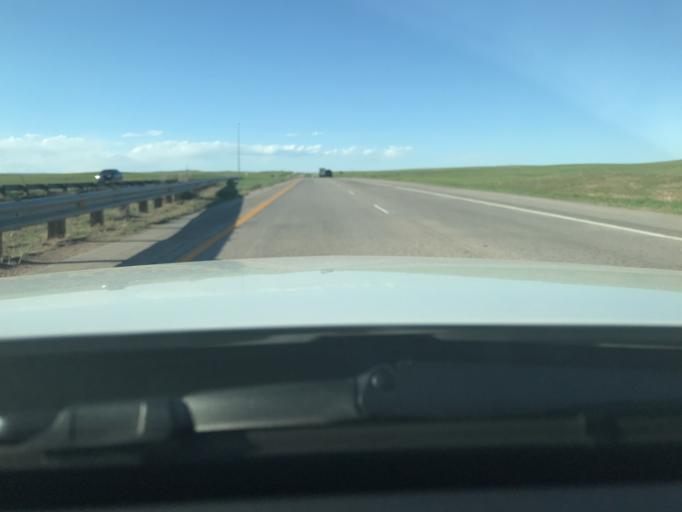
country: US
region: Colorado
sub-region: Larimer County
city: Wellington
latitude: 40.8413
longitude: -104.9661
